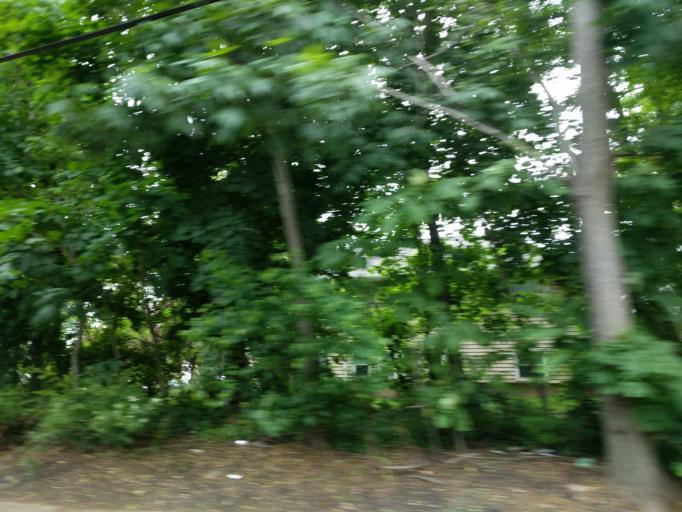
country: US
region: New York
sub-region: Nassau County
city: Cedarhurst
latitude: 40.6324
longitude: -73.7250
